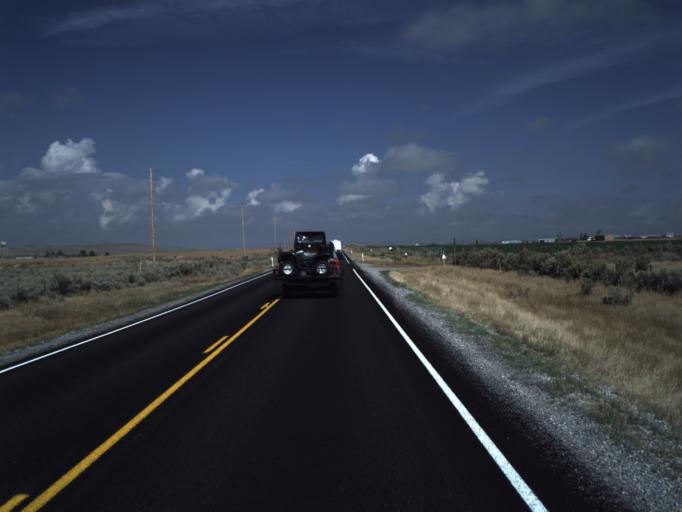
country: US
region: Utah
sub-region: Rich County
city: Randolph
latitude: 41.5756
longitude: -111.1633
